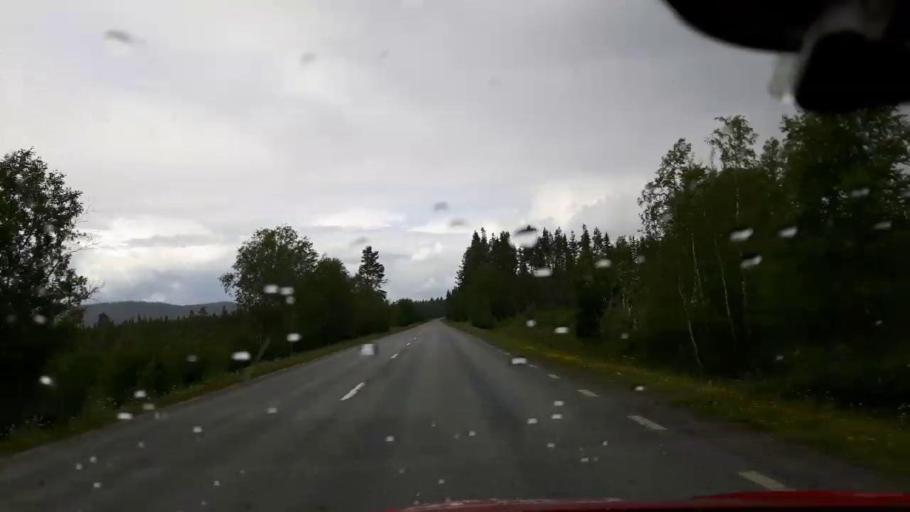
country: SE
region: Jaemtland
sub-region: Krokoms Kommun
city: Krokom
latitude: 63.4402
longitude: 14.1989
